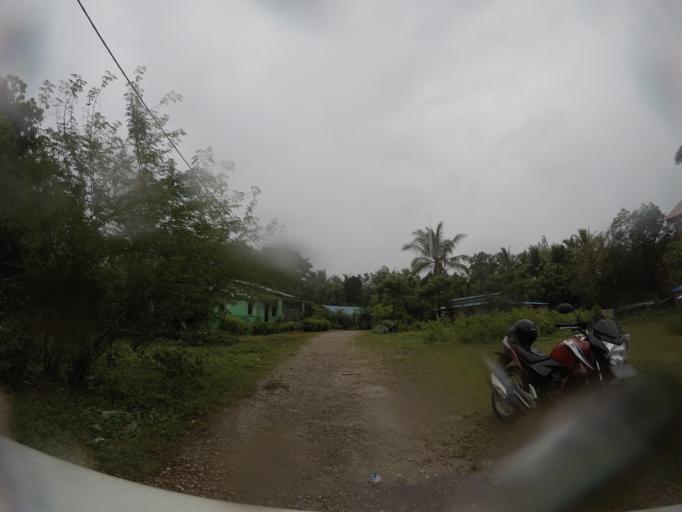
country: TL
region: Lautem
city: Lospalos
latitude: -8.5192
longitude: 126.9999
